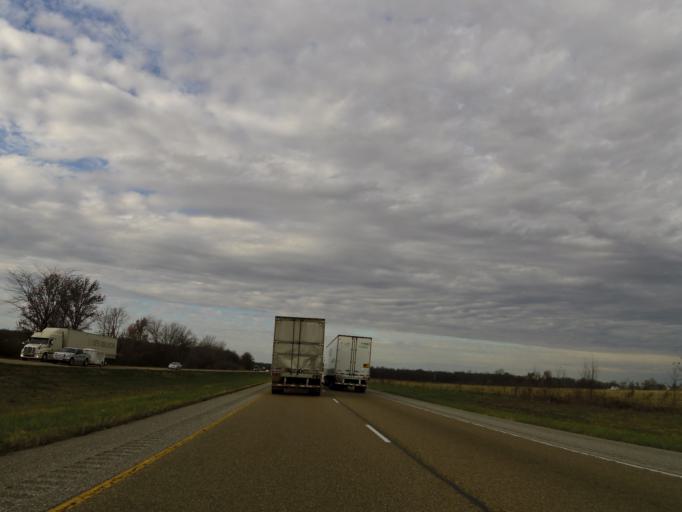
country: US
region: Illinois
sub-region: Washington County
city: Nashville
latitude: 38.3913
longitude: -89.2884
